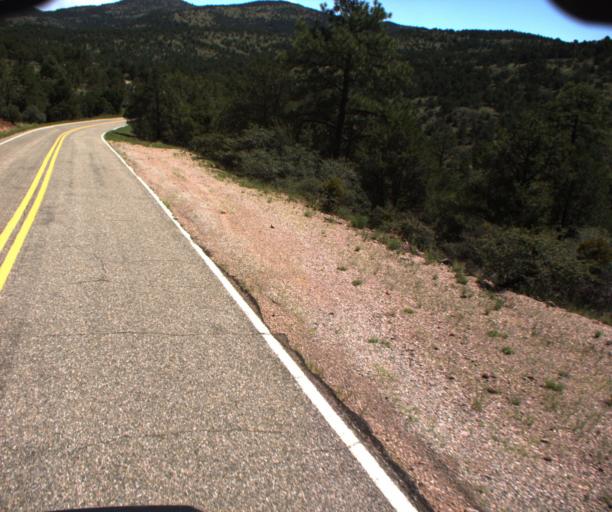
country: US
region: Arizona
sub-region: Greenlee County
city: Morenci
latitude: 33.3530
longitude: -109.3457
